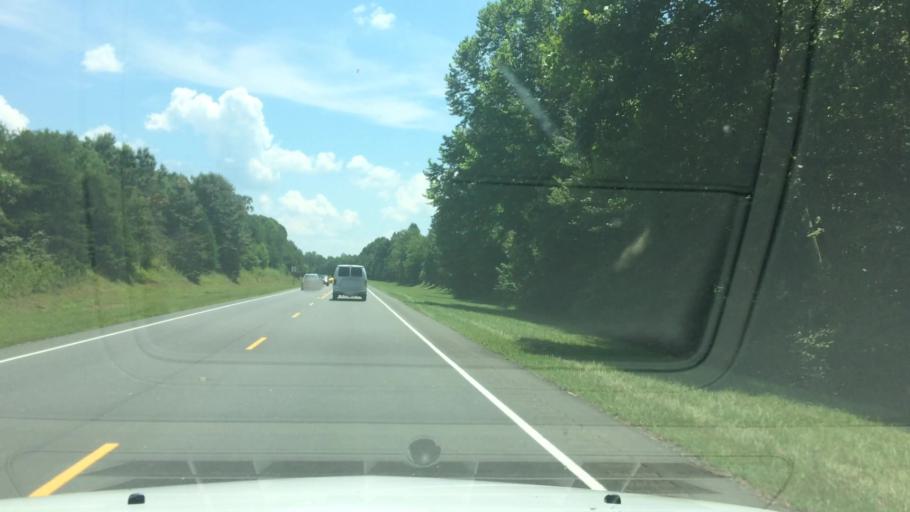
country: US
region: North Carolina
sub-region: Alexander County
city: Stony Point
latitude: 35.8295
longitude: -81.0149
